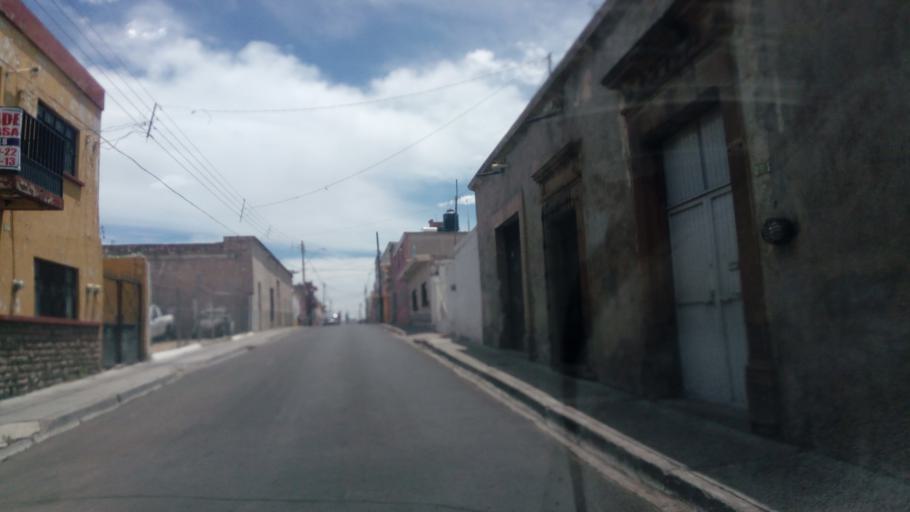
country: MX
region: Durango
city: Victoria de Durango
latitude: 24.0154
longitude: -104.6701
